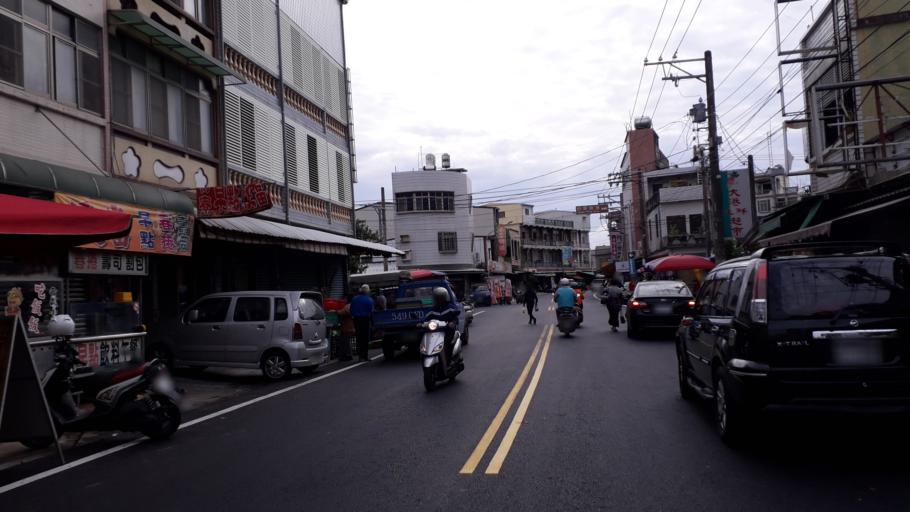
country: TW
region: Taiwan
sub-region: Pingtung
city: Pingtung
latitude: 22.3632
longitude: 120.5963
